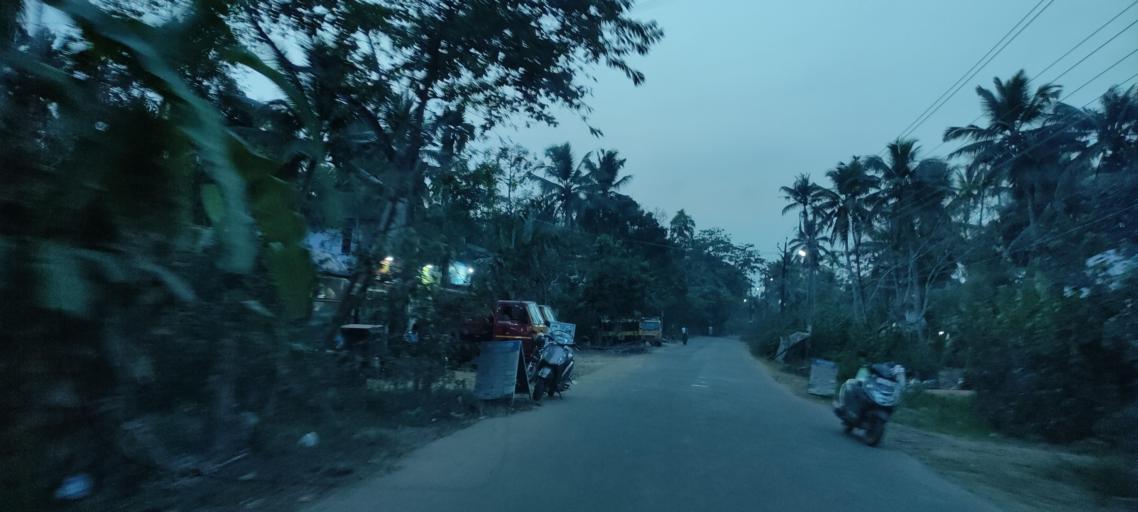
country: IN
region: Kerala
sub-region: Alappuzha
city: Mavelikara
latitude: 9.3298
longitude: 76.4721
